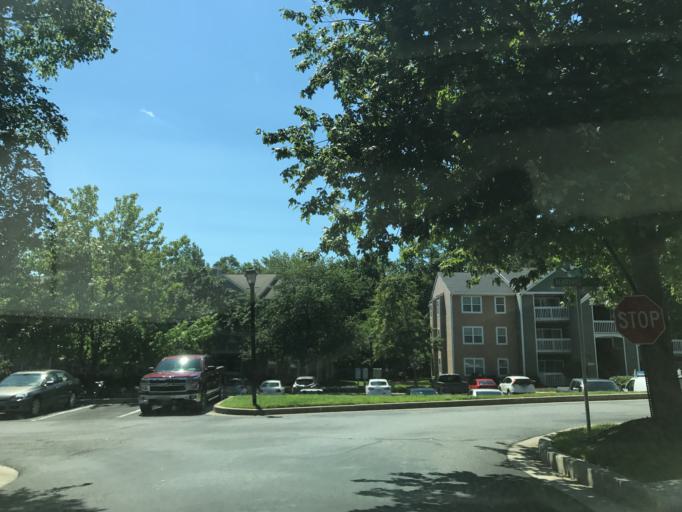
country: US
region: Maryland
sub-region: Baltimore County
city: White Marsh
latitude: 39.3806
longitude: -76.4561
